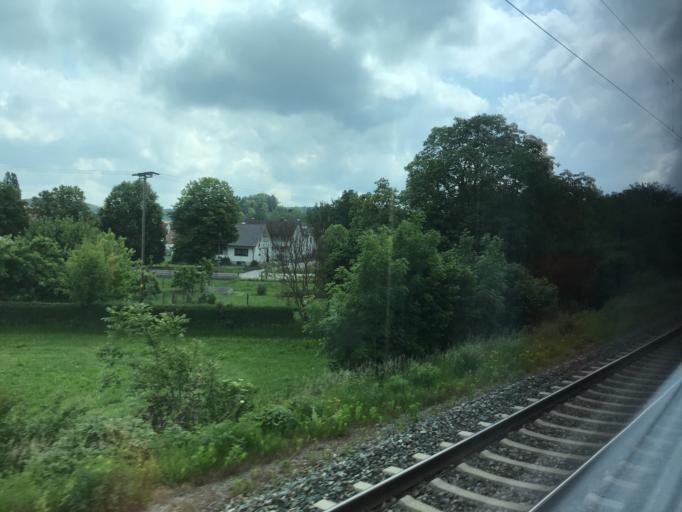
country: DE
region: Bavaria
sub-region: Swabia
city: Jettingen-Scheppach
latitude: 48.4027
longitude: 10.4405
